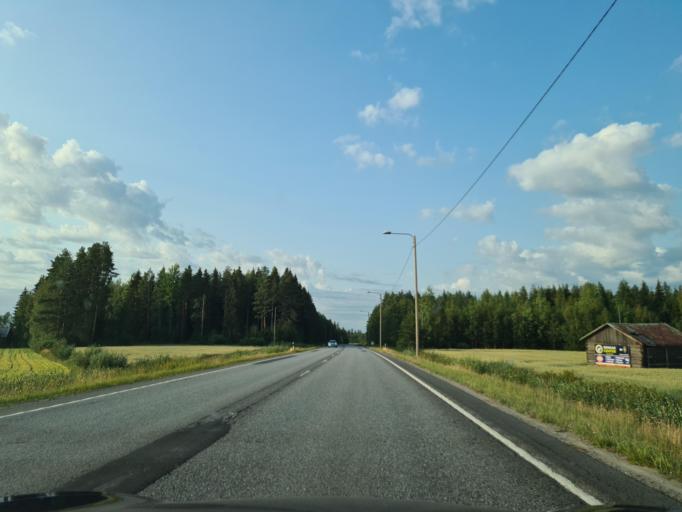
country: FI
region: Southern Ostrobothnia
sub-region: Seinaejoki
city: Kauhava
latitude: 63.0634
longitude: 23.0427
